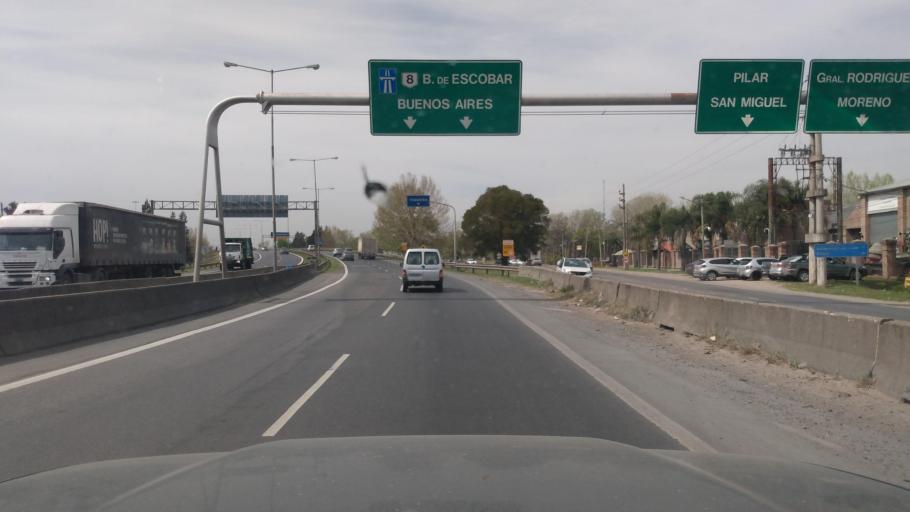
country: AR
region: Buenos Aires
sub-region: Partido de Pilar
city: Pilar
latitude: -34.4530
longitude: -58.9431
